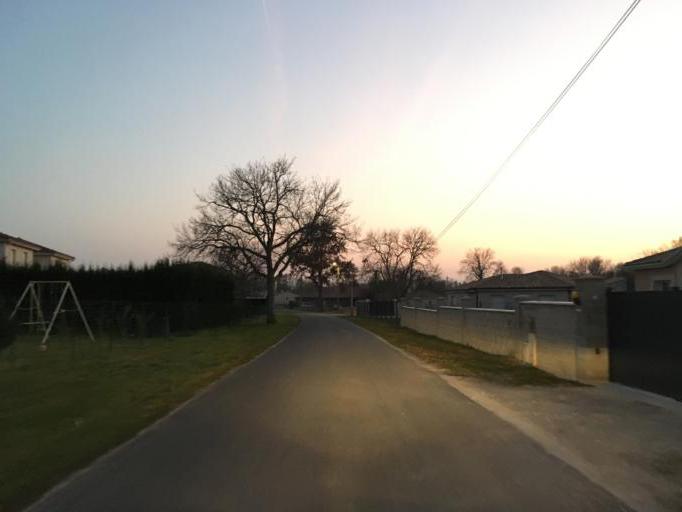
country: FR
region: Aquitaine
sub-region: Departement de la Gironde
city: Braud-et-Saint-Louis
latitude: 45.2567
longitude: -0.6237
